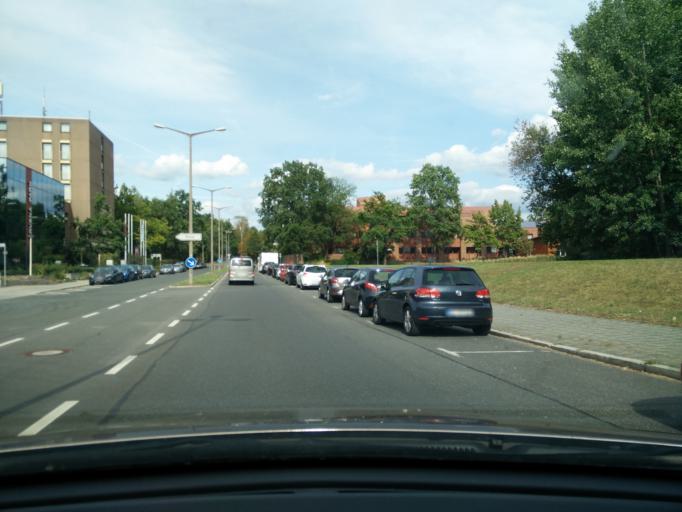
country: DE
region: Bavaria
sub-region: Regierungsbezirk Mittelfranken
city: Wendelstein
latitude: 49.3996
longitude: 11.1370
